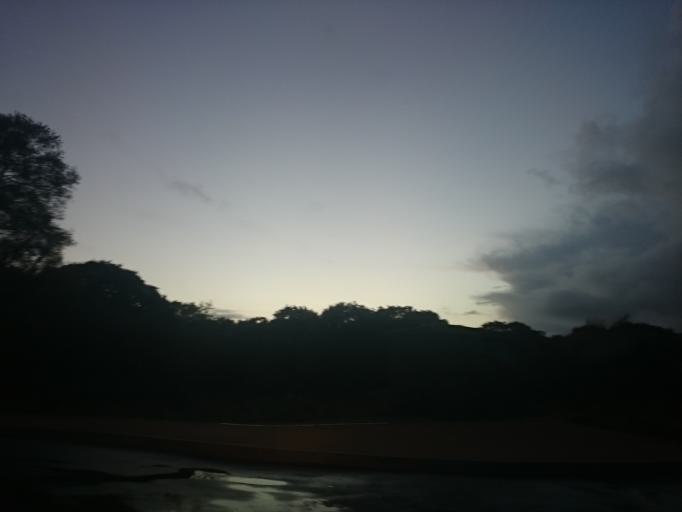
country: FR
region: Brittany
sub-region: Departement du Finistere
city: Brest
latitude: 48.4210
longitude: -4.4690
